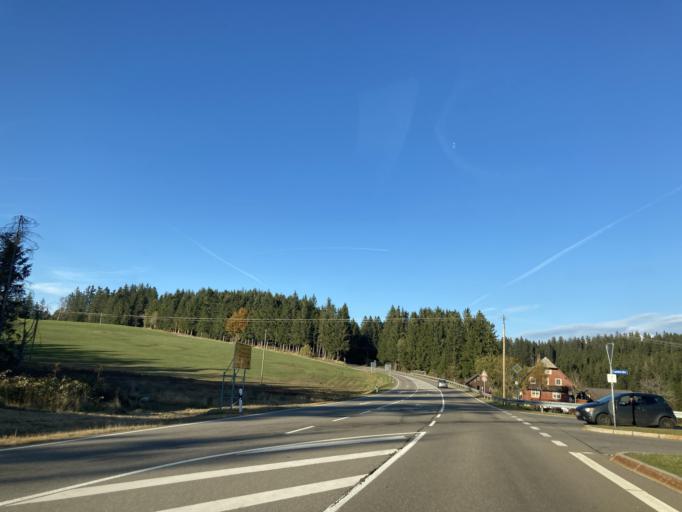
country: DE
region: Baden-Wuerttemberg
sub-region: Freiburg Region
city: Sankt Margen
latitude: 47.9847
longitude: 8.1521
